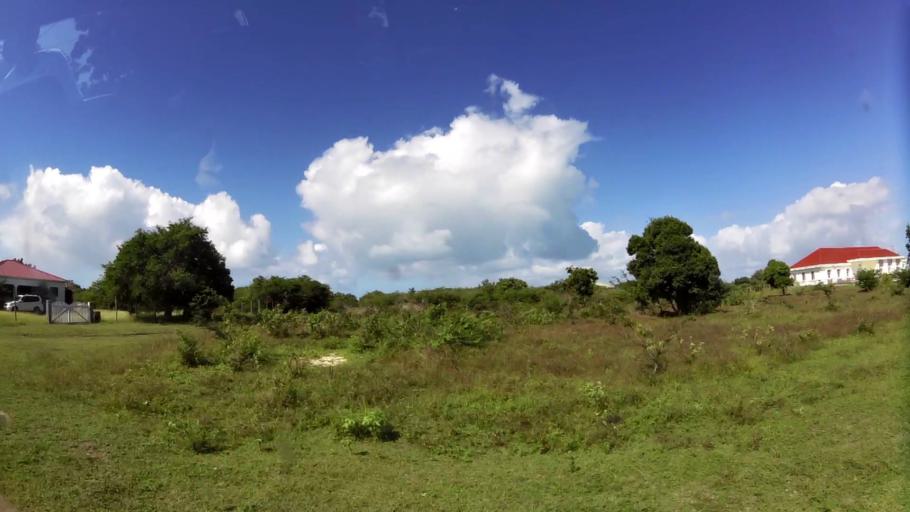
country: AG
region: Barbuda
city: Codrington
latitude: 17.6267
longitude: -61.8274
